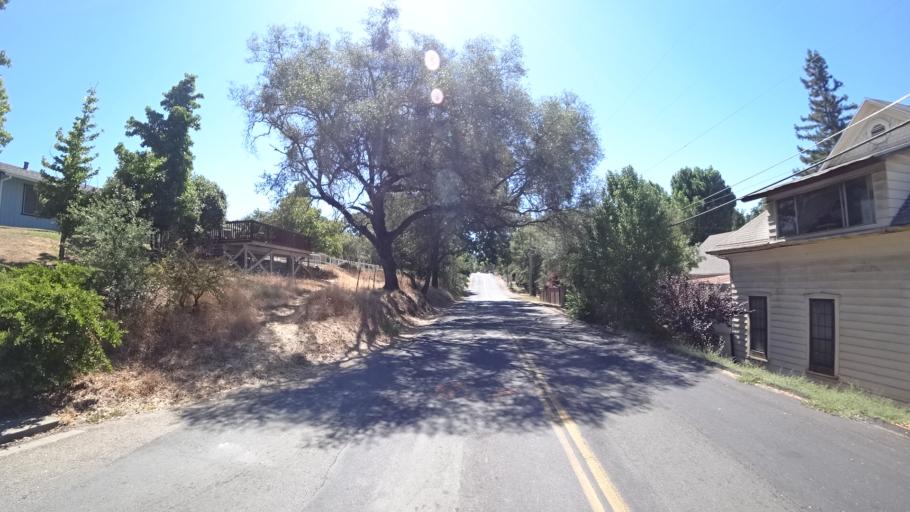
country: US
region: California
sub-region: Calaveras County
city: San Andreas
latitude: 38.1977
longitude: -120.6784
